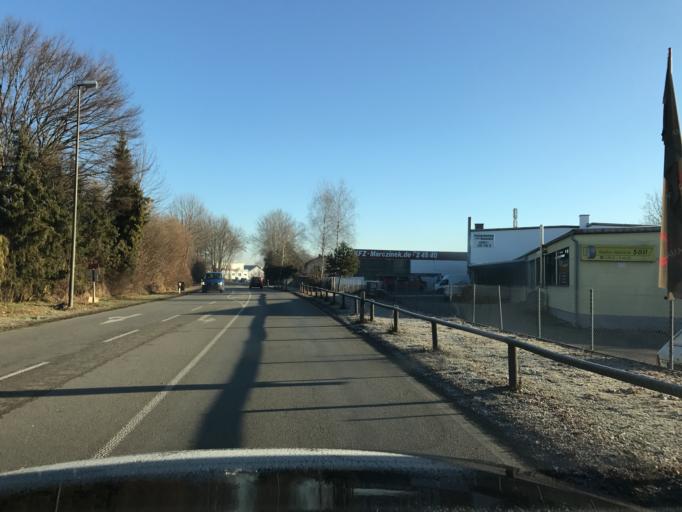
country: DE
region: Bavaria
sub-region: Upper Bavaria
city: Kolbermoor
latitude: 47.8423
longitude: 12.0478
